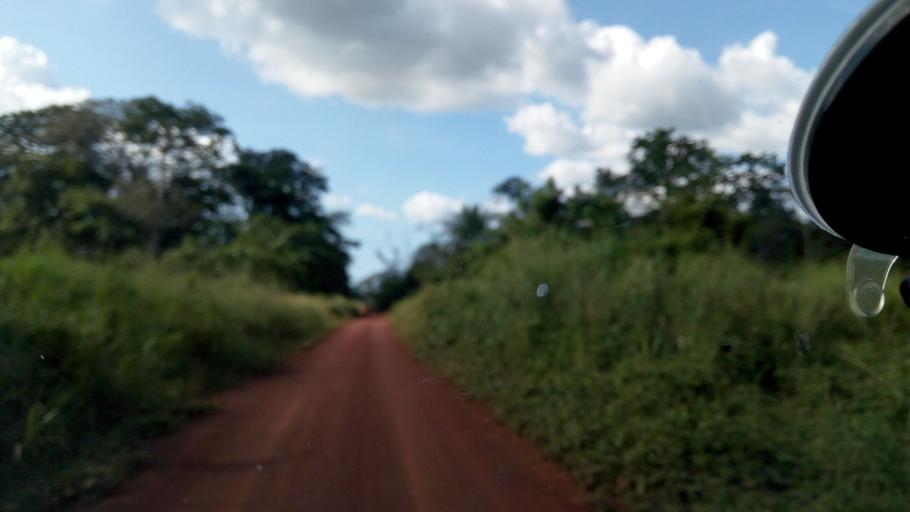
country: CD
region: Equateur
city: Libenge
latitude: 3.8001
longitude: 18.7051
